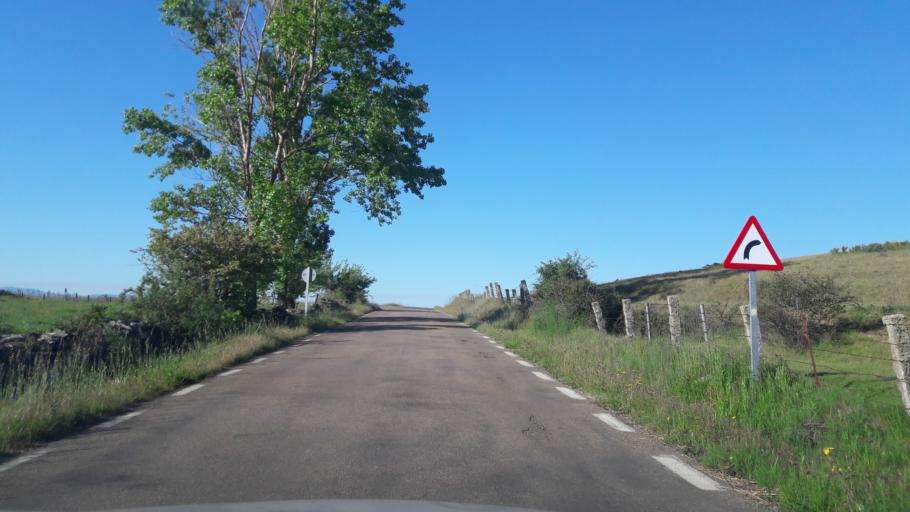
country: ES
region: Castille and Leon
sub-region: Provincia de Salamanca
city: Herguijuela del Campo
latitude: 40.6288
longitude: -5.8635
